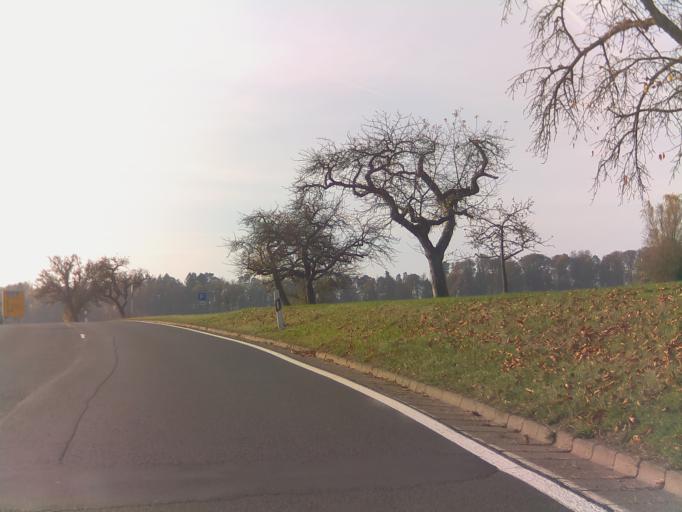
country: DE
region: Bavaria
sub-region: Regierungsbezirk Unterfranken
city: Oberthulba
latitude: 50.2396
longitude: 9.9641
